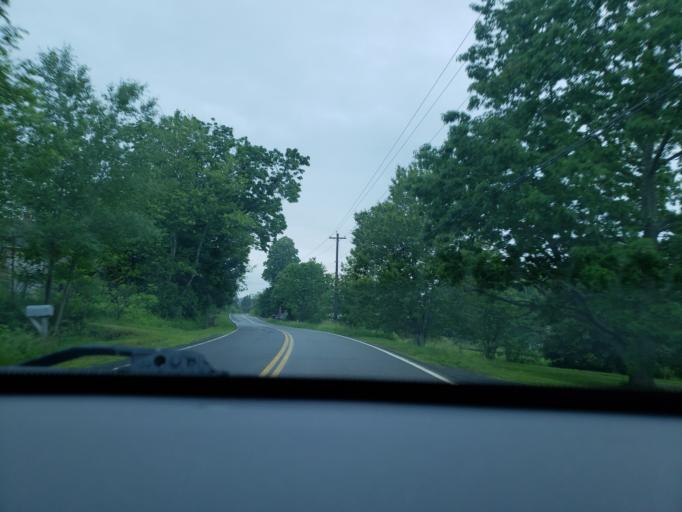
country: CA
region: Nova Scotia
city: Windsor
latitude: 45.0606
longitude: -63.9913
